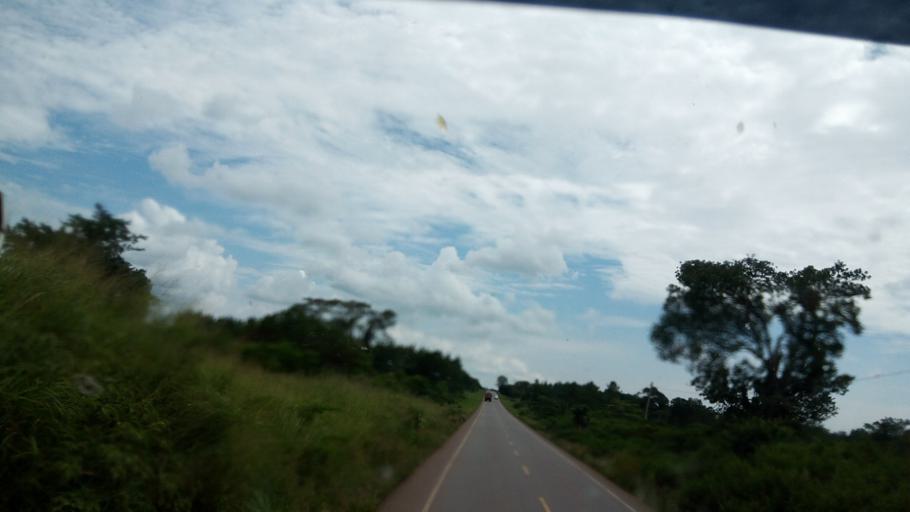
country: UG
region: Central Region
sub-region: Nakasongola District
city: Nakasongola
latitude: 1.1709
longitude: 32.4629
